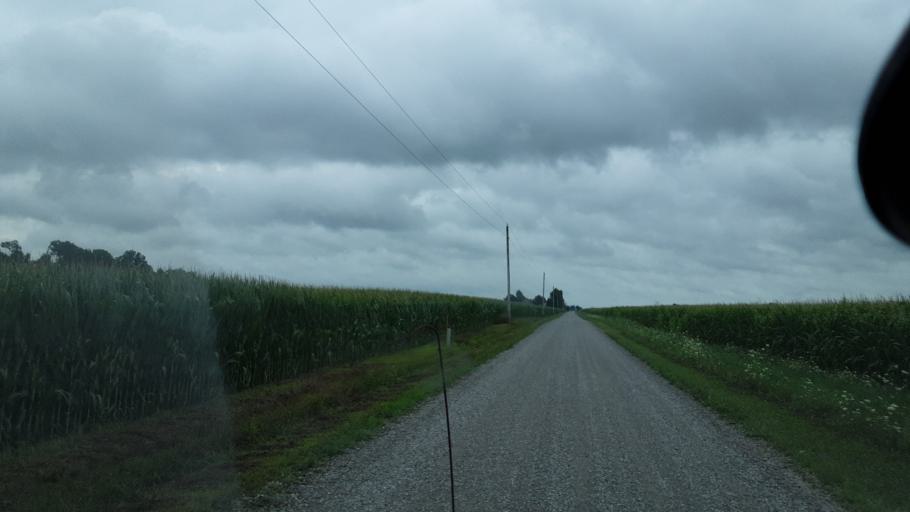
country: US
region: Indiana
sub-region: Wells County
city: Bluffton
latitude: 40.7828
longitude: -85.0718
